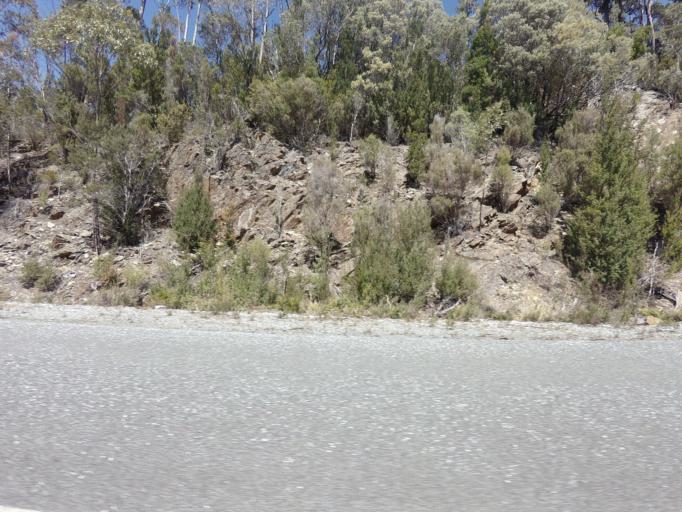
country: AU
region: Tasmania
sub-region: West Coast
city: Queenstown
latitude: -42.7683
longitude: 146.0168
